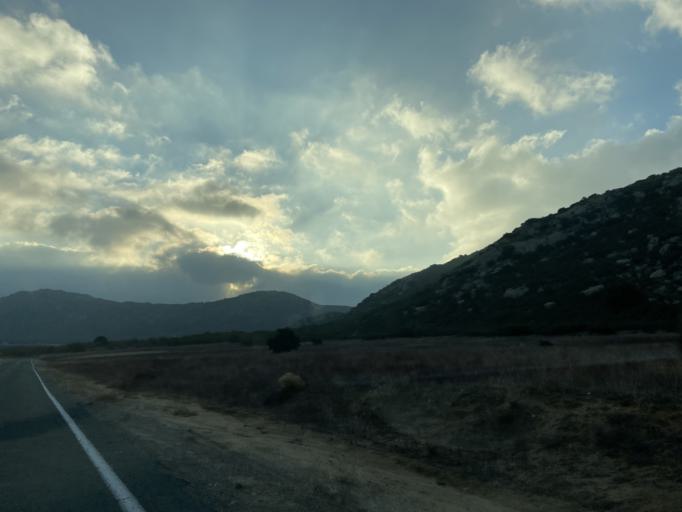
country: US
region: California
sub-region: San Diego County
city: Pine Valley
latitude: 32.7241
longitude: -116.4653
